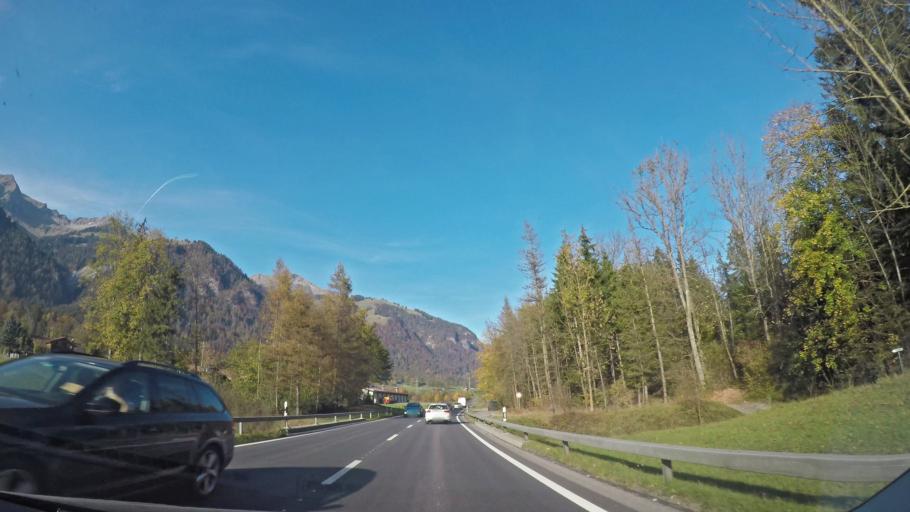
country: CH
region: Bern
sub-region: Frutigen-Niedersimmental District
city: Frutigen
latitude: 46.6004
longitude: 7.6610
